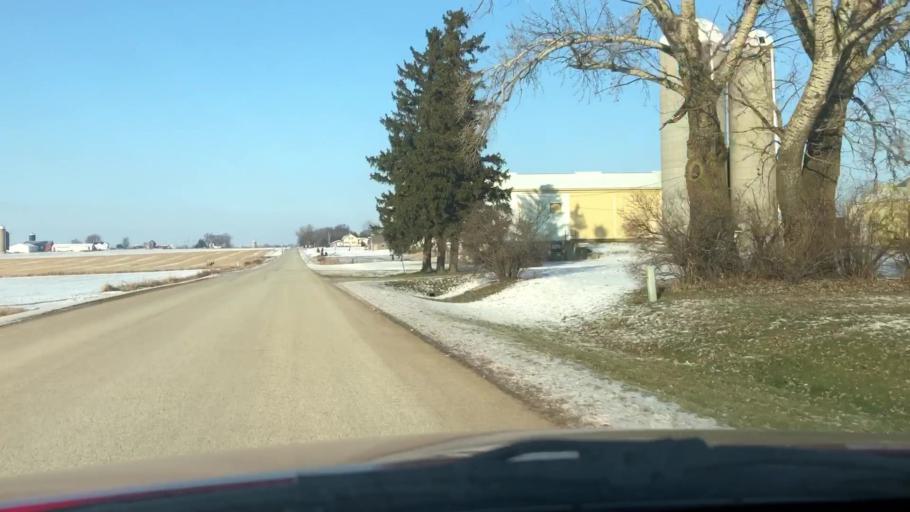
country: US
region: Wisconsin
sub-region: Outagamie County
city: Seymour
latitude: 44.4913
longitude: -88.3090
